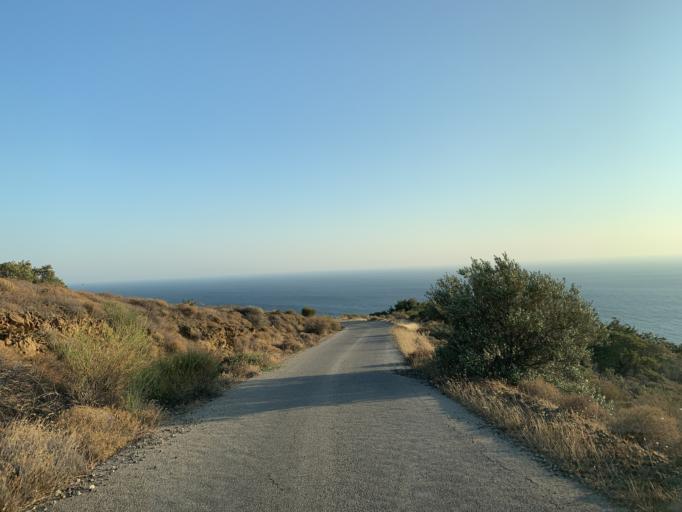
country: GR
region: North Aegean
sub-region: Chios
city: Psara
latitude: 38.5247
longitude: 25.8520
